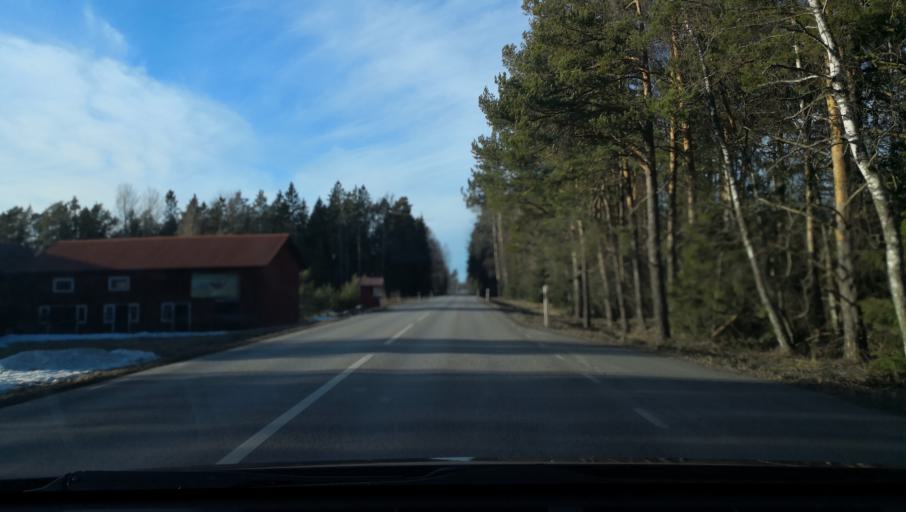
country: SE
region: Uppsala
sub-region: Osthammars Kommun
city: OEsthammar
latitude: 60.2764
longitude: 18.3037
